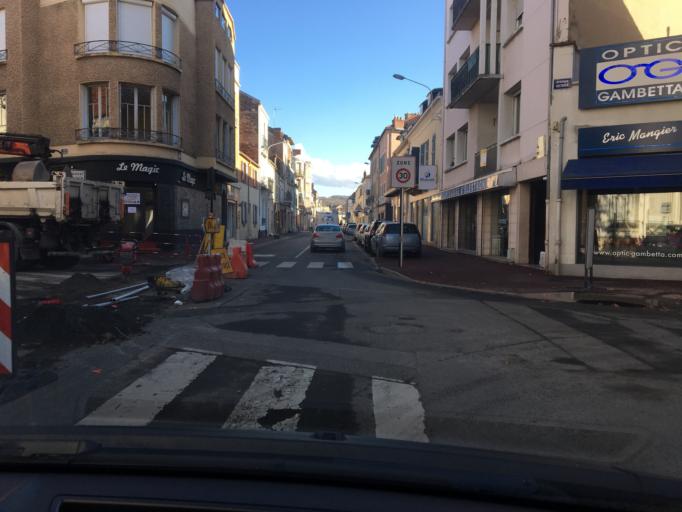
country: FR
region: Auvergne
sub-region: Departement de l'Allier
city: Vichy
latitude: 46.1286
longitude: 3.4266
